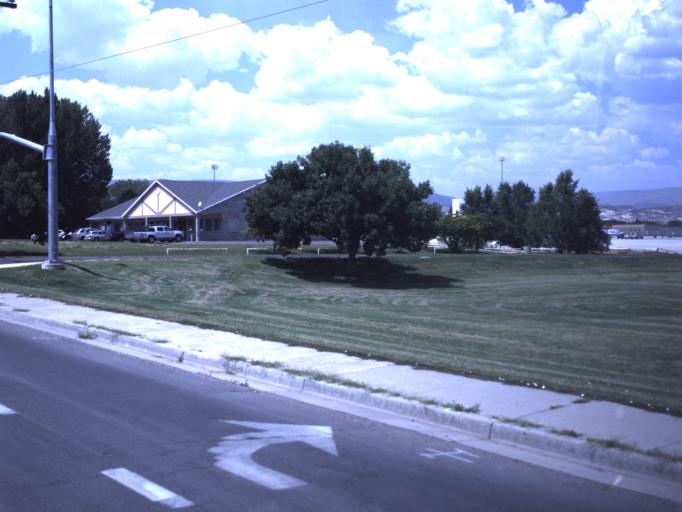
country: US
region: Utah
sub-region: Uintah County
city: Maeser
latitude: 40.4627
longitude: -109.5662
